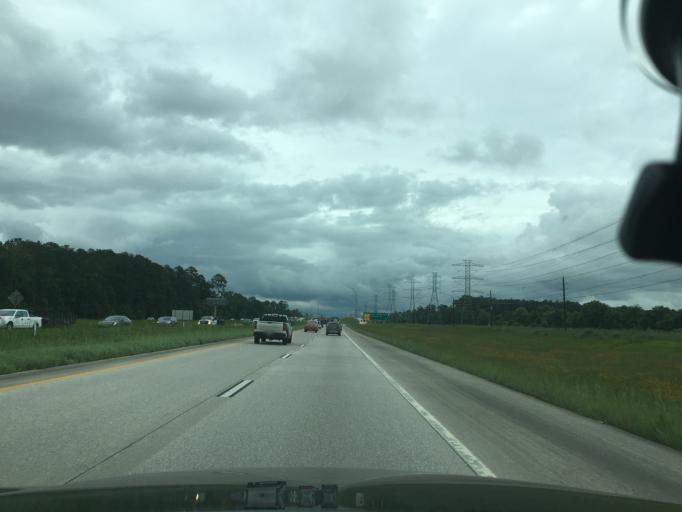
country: US
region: Texas
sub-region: Harris County
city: Spring
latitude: 30.0905
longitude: -95.4660
